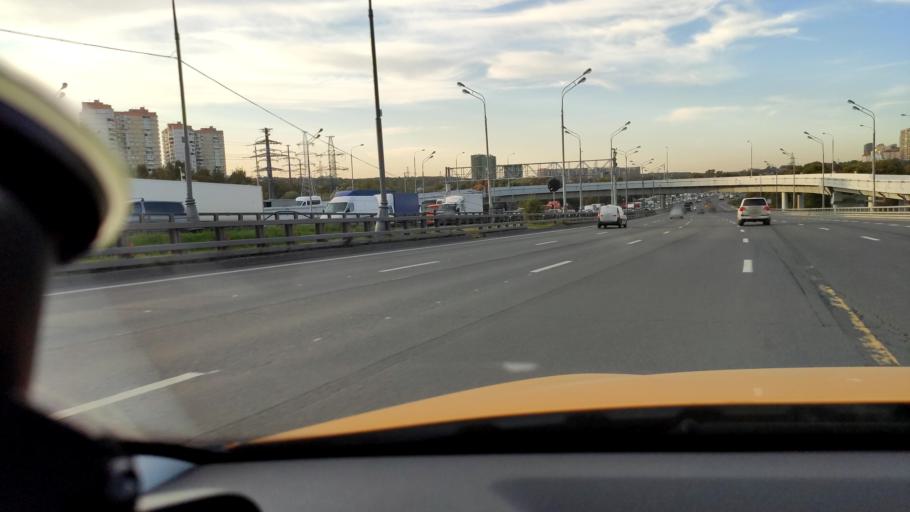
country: RU
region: Moscow
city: Strogino
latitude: 55.8405
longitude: 37.3933
